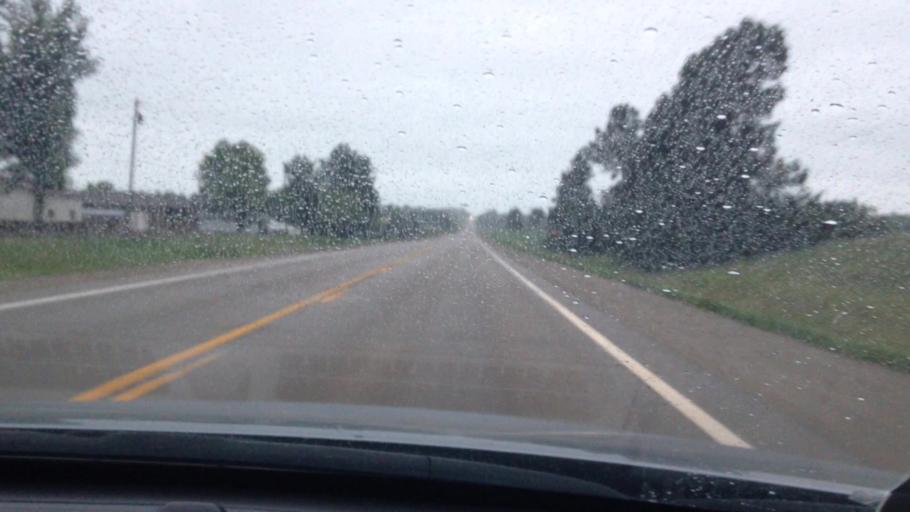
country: US
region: Kansas
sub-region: Brown County
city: Hiawatha
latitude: 39.8352
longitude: -95.5270
